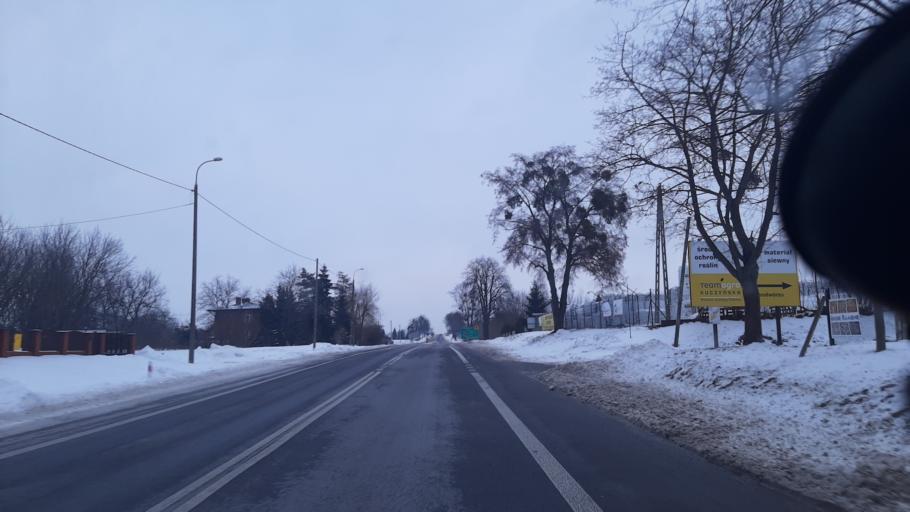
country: PL
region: Lublin Voivodeship
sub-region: Powiat pulawski
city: Markuszow
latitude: 51.3720
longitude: 22.2717
